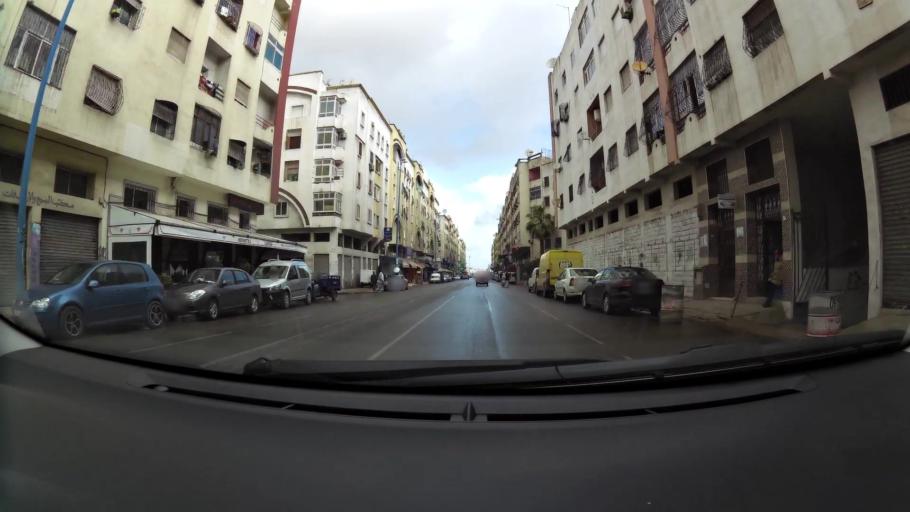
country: MA
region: Grand Casablanca
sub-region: Mediouna
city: Tit Mellil
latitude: 33.5922
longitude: -7.5171
